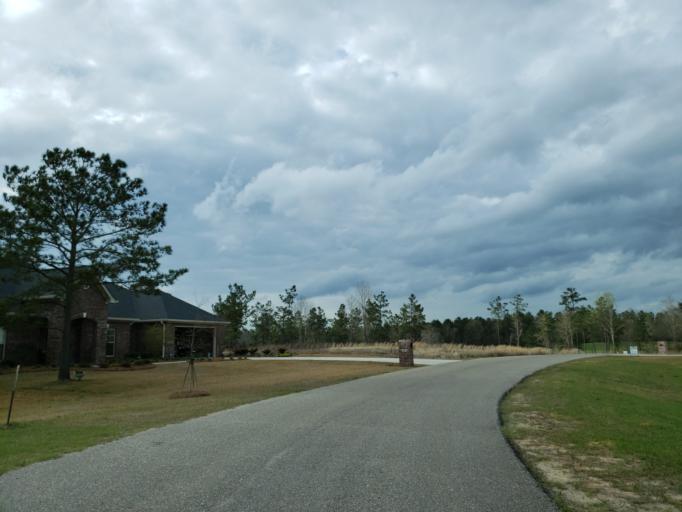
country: US
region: Mississippi
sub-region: Jones County
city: Ellisville
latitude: 31.5557
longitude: -89.2579
